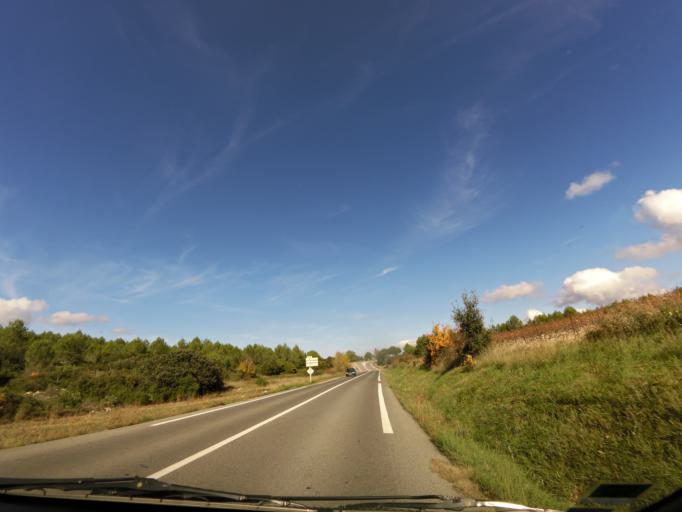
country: FR
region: Languedoc-Roussillon
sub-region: Departement du Gard
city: Villevieille
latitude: 43.8675
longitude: 4.0989
